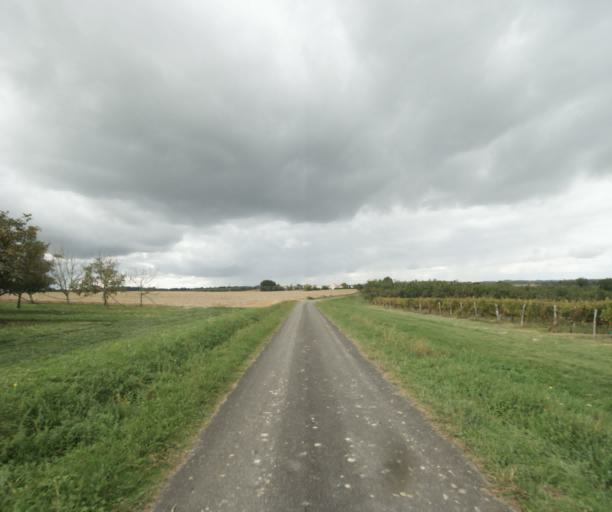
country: FR
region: Midi-Pyrenees
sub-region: Departement du Gers
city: Eauze
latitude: 43.8730
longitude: 0.0659
